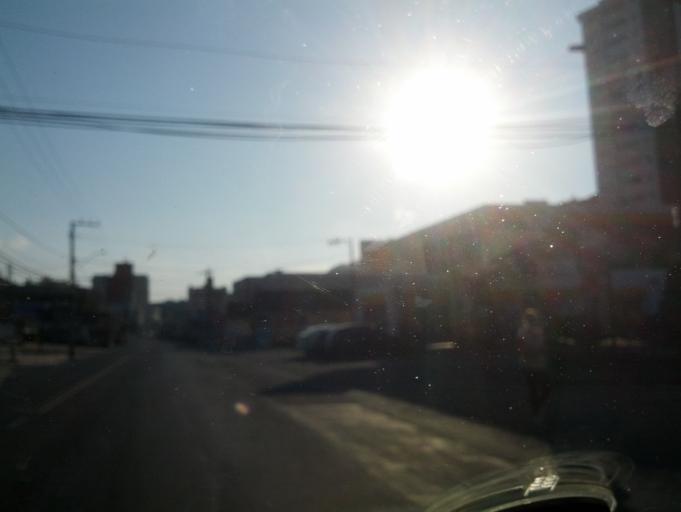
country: BR
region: Santa Catarina
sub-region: Blumenau
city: Blumenau
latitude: -26.9114
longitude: -49.0892
